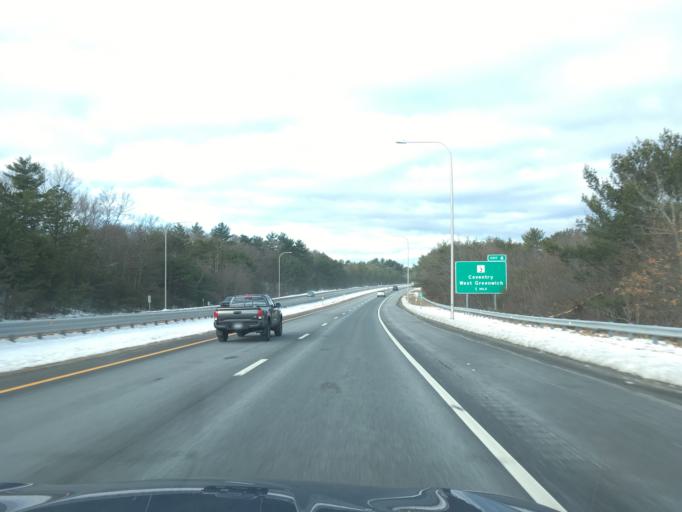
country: US
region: Rhode Island
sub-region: Kent County
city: West Warwick
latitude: 41.6503
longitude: -71.5833
